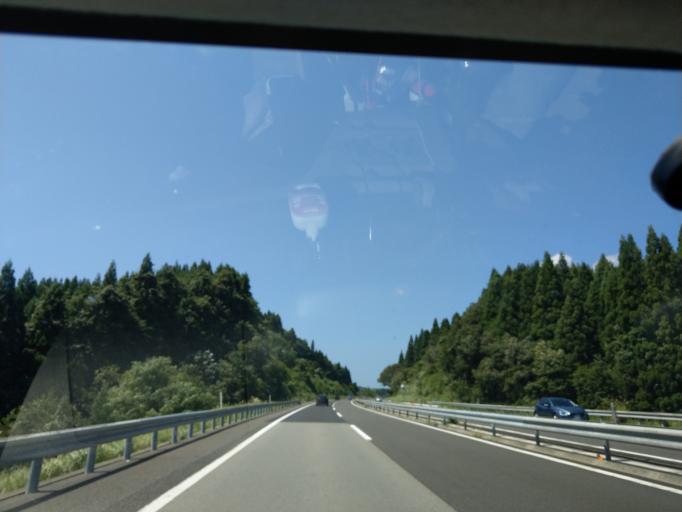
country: JP
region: Akita
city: Akita
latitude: 39.6241
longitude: 140.2374
